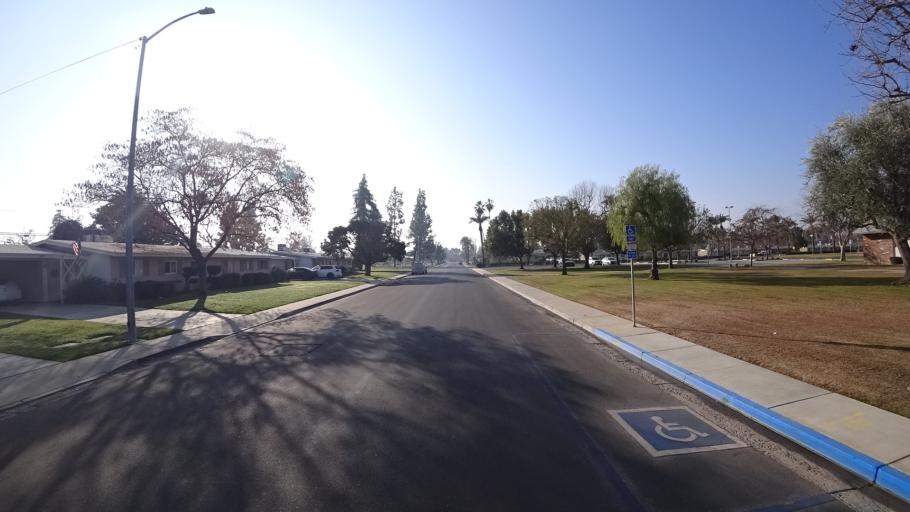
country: US
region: California
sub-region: Kern County
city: Bakersfield
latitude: 35.3449
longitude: -119.0666
